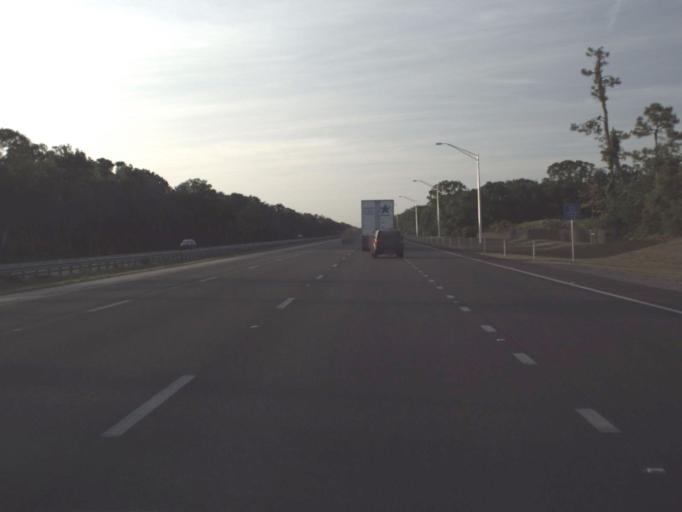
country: US
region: Florida
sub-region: Brevard County
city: Mims
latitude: 28.6903
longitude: -80.8795
